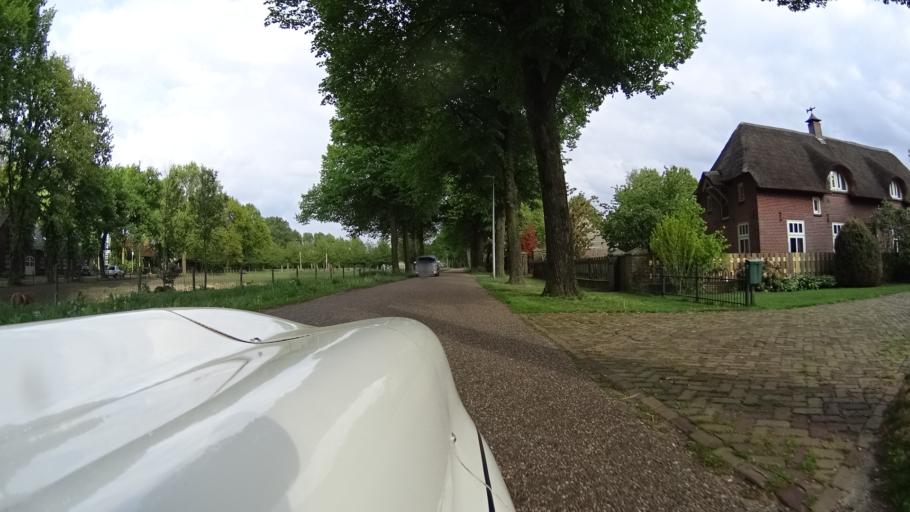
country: NL
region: North Brabant
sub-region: Gemeente Uden
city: Volkel
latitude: 51.6350
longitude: 5.6680
